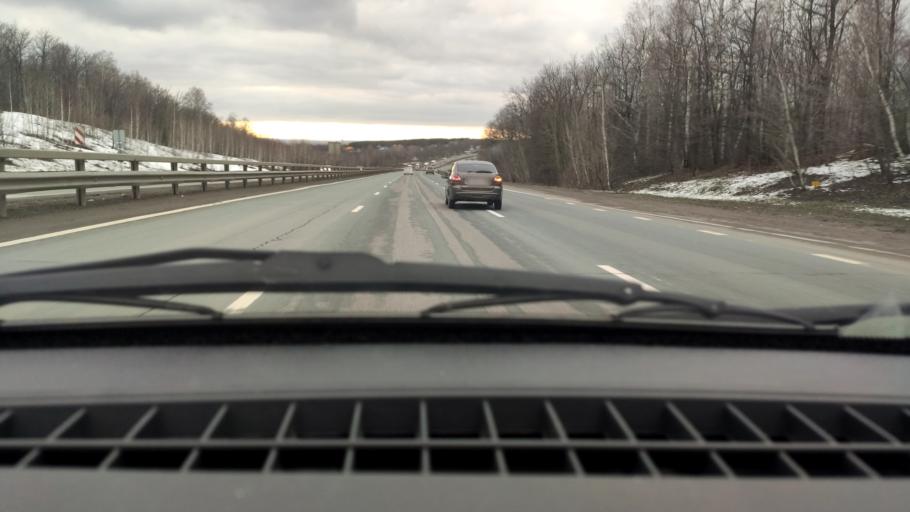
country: RU
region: Bashkortostan
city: Avdon
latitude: 54.6411
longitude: 55.6054
